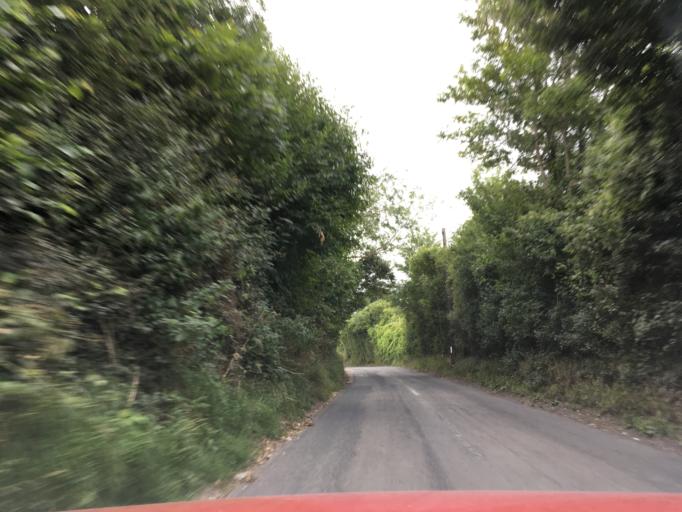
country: GB
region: England
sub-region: Kent
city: Yalding
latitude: 51.2407
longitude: 0.4494
